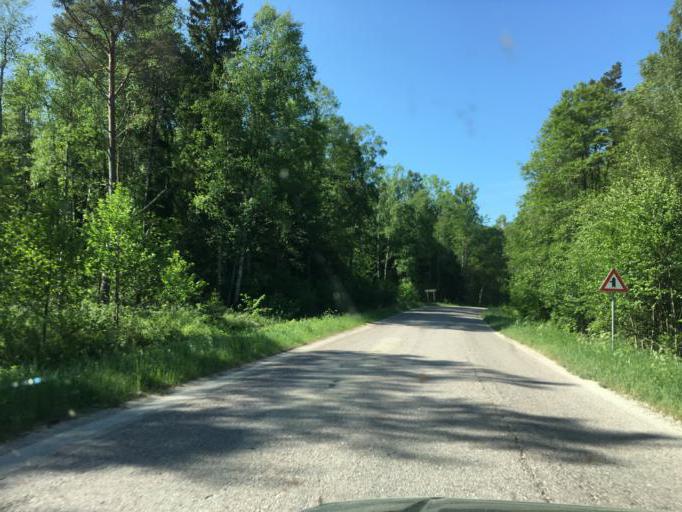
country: LV
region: Ventspils
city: Ventspils
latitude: 57.4932
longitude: 21.8091
